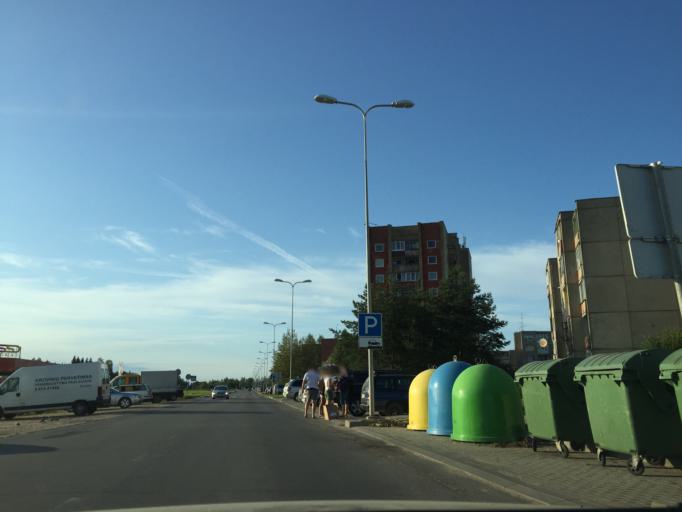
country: LT
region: Panevezys
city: Rokiskis
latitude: 55.9448
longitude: 25.5819
